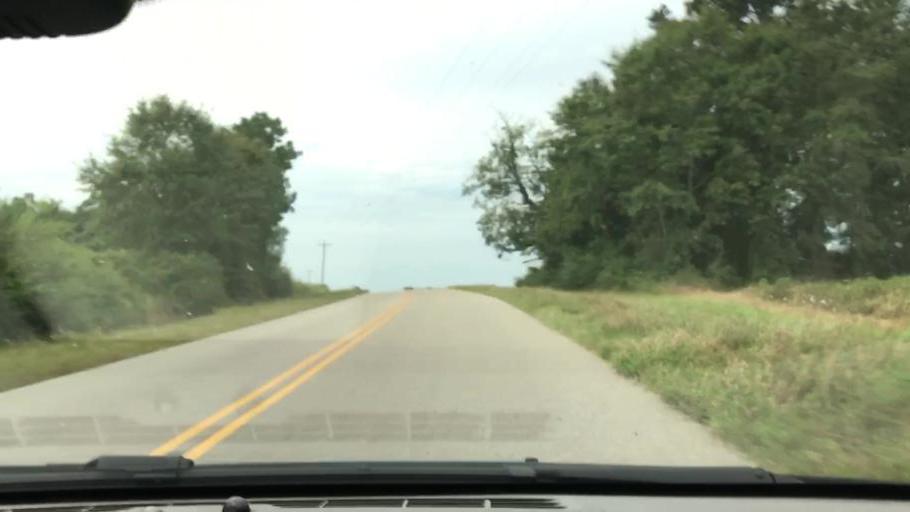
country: US
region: Alabama
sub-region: Houston County
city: Ashford
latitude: 31.2444
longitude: -85.1722
